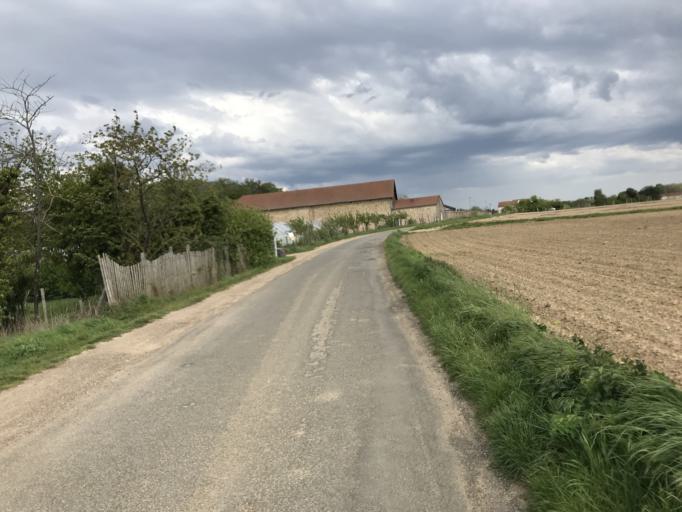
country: FR
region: Ile-de-France
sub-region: Departement de l'Essonne
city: Vauhallan
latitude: 48.7290
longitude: 2.1985
